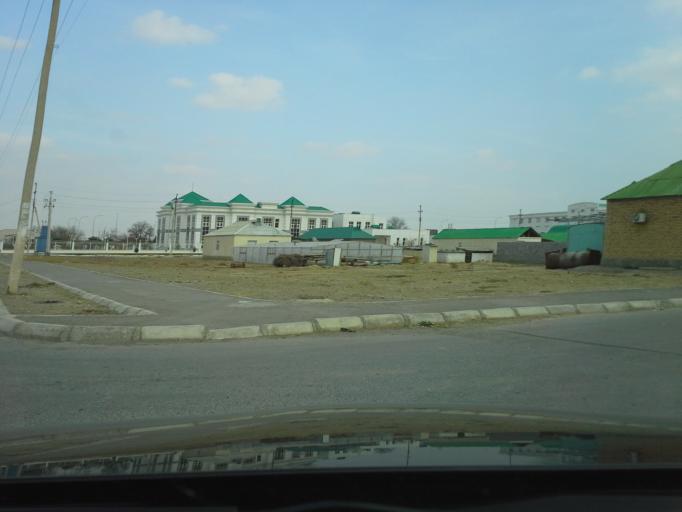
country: TM
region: Ahal
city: Abadan
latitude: 38.0351
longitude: 58.2656
